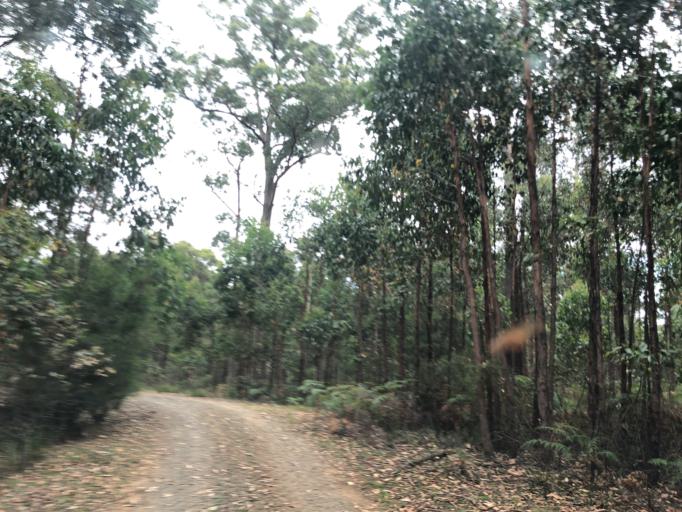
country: AU
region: Victoria
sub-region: Moorabool
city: Bacchus Marsh
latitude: -37.4415
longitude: 144.2468
